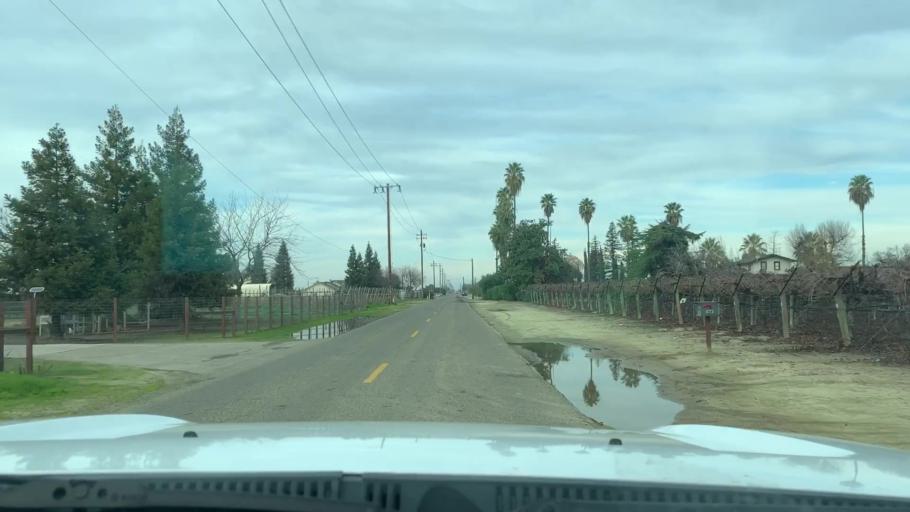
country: US
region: California
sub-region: Fresno County
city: Selma
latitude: 36.5634
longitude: -119.5750
